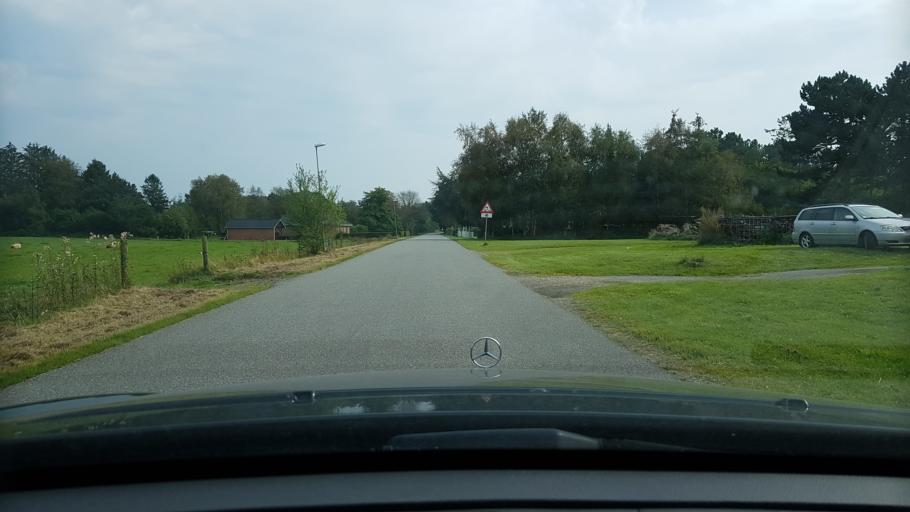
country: DK
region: North Denmark
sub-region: Alborg Kommune
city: Hals
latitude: 56.9619
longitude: 10.2260
